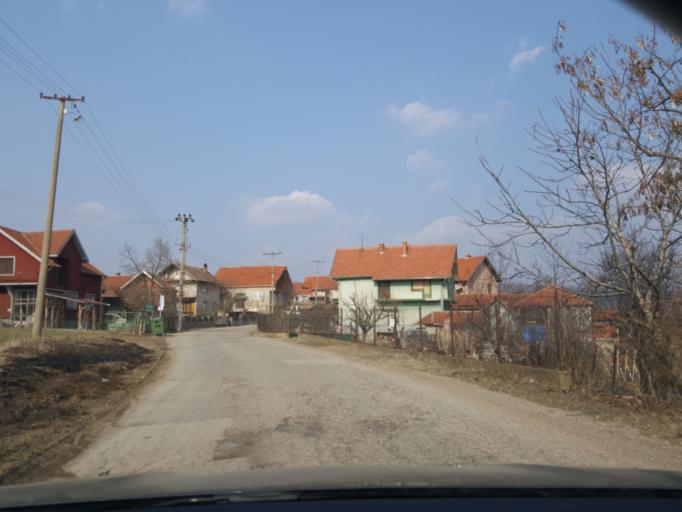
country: RS
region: Central Serbia
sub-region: Nisavski Okrug
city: Aleksinac
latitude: 43.5238
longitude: 21.7339
